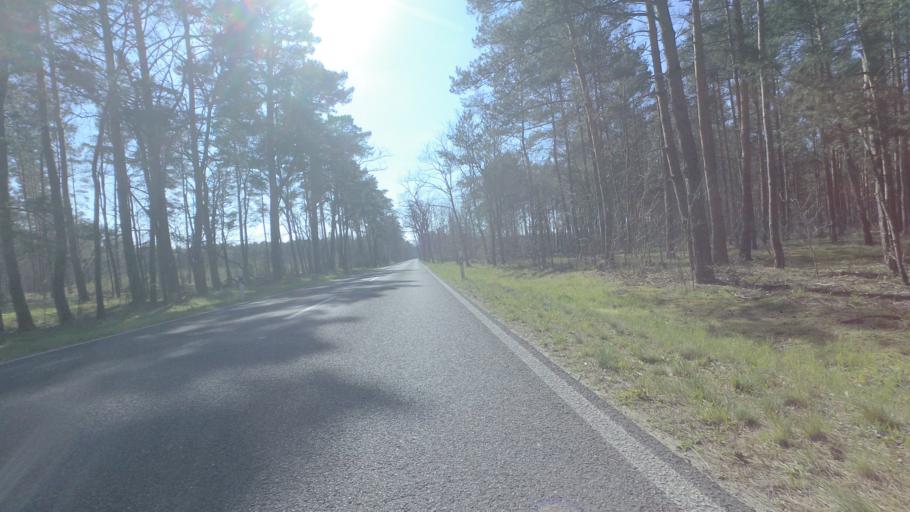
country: DE
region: Brandenburg
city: Munchehofe
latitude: 52.1216
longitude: 13.7955
